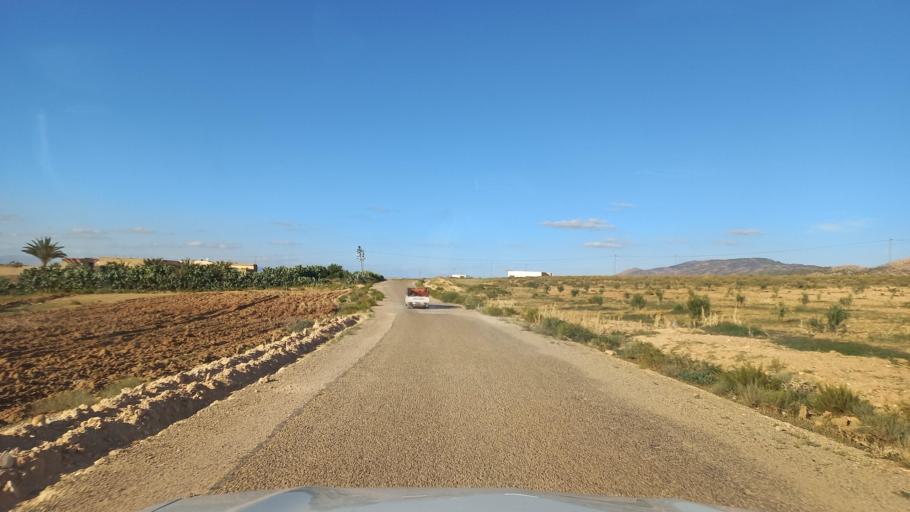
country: TN
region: Al Qasrayn
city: Sbiba
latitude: 35.3539
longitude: 9.1365
